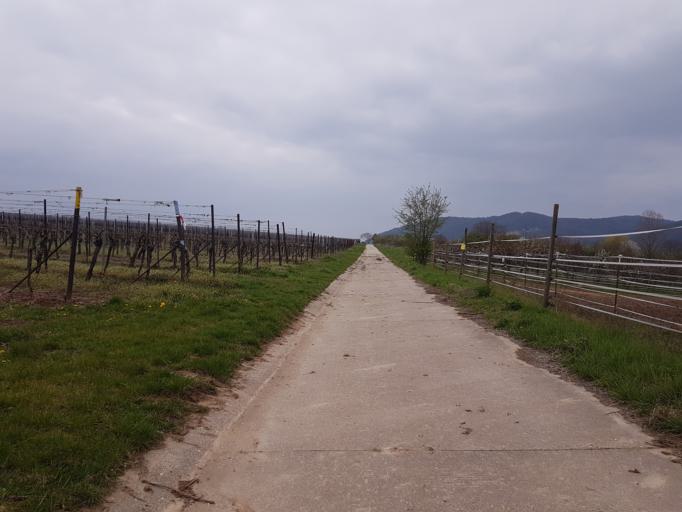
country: DE
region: Rheinland-Pfalz
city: Bochingen
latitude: 49.2286
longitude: 8.0853
